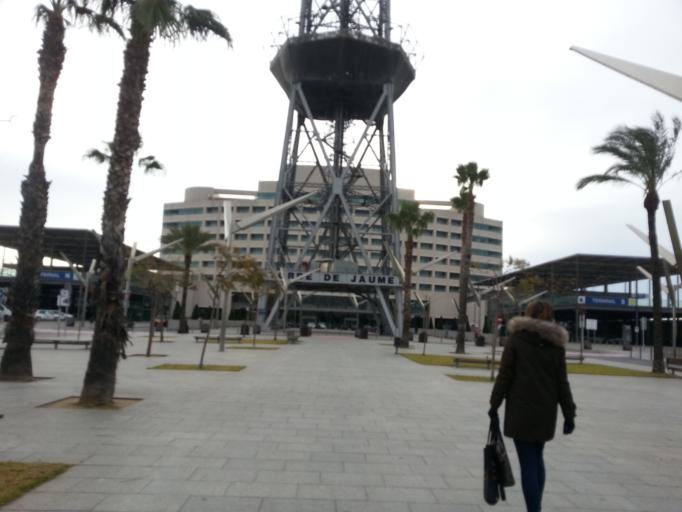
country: ES
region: Catalonia
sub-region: Provincia de Barcelona
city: Ciutat Vella
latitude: 41.3725
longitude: 2.1793
